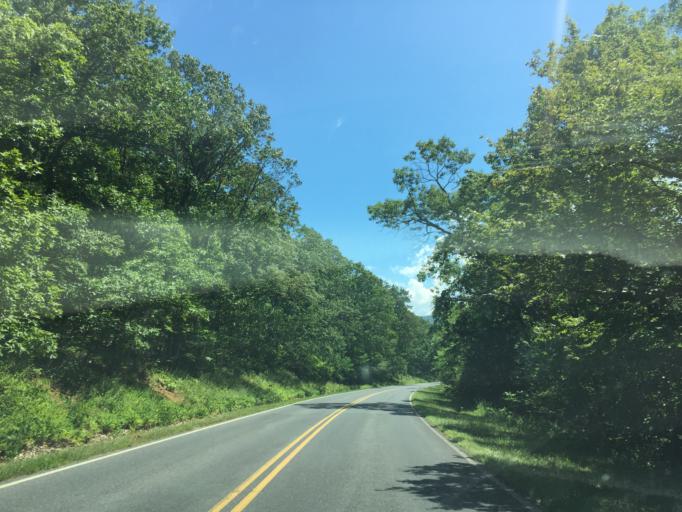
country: US
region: Virginia
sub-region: Warren County
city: Front Royal
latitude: 38.8396
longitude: -78.2051
